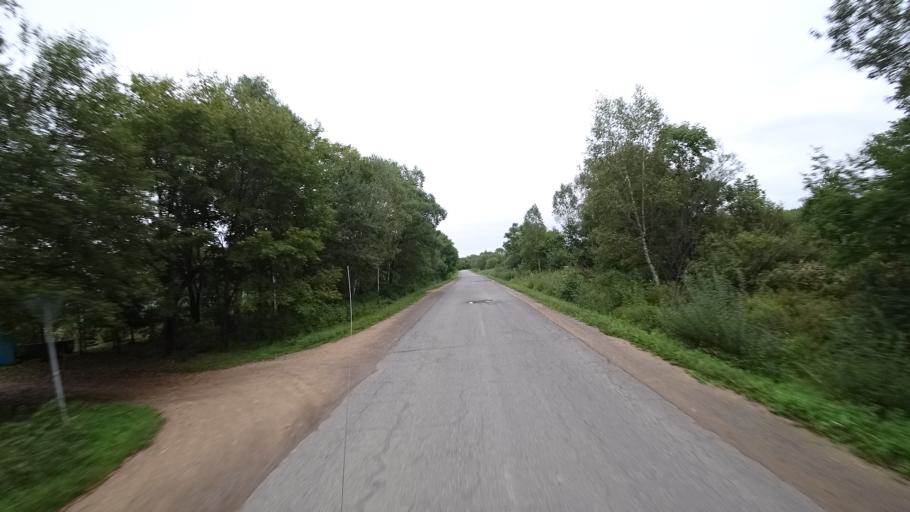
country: RU
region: Primorskiy
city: Rettikhovka
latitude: 44.1655
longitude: 132.7744
